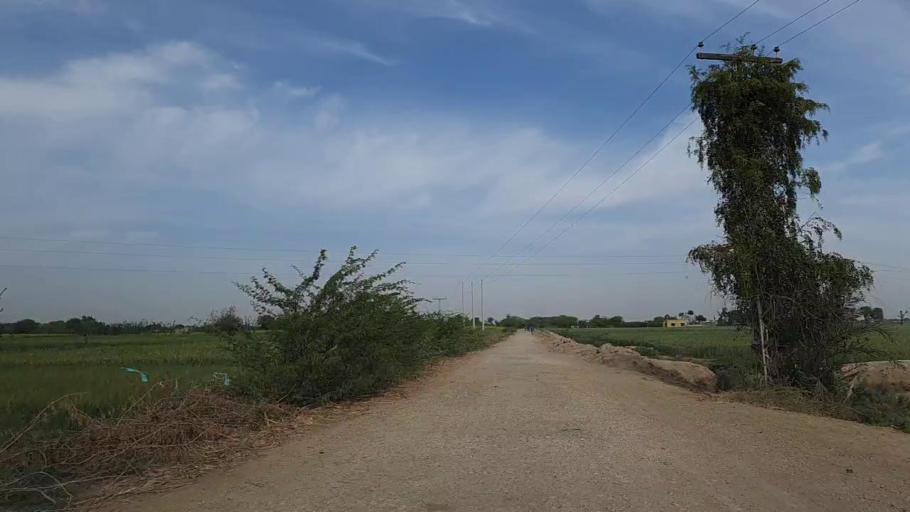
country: PK
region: Sindh
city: Samaro
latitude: 25.2967
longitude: 69.4239
